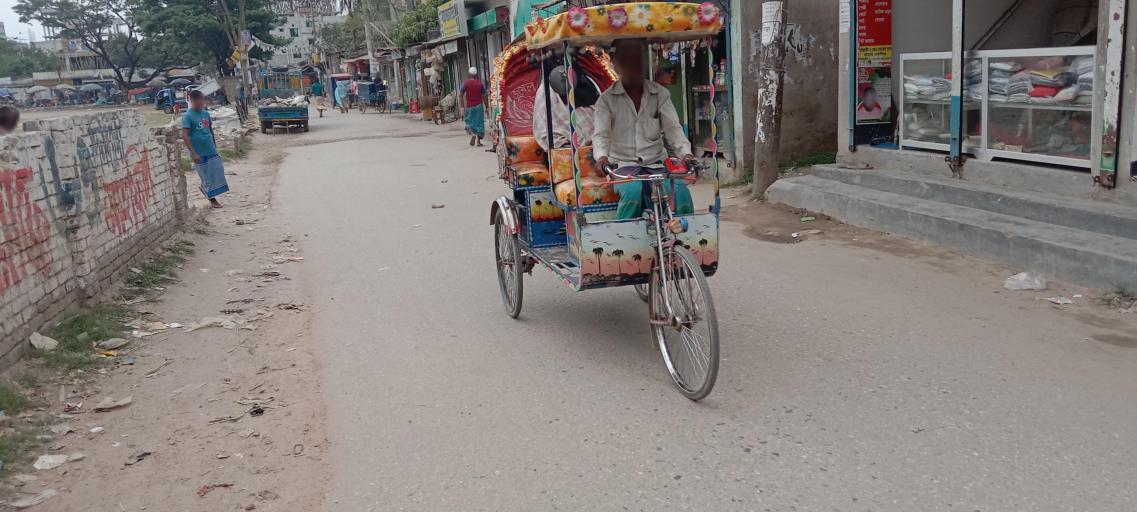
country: BD
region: Dhaka
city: Azimpur
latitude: 23.7364
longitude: 90.3347
